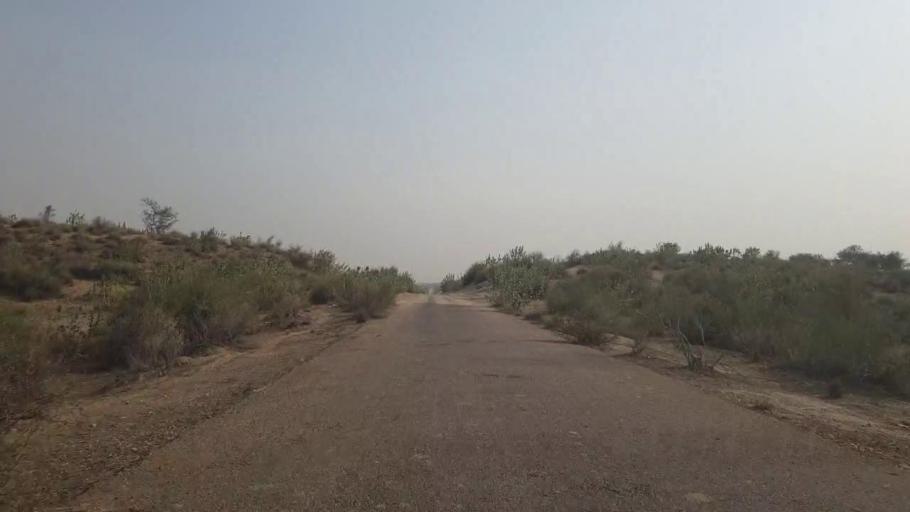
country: PK
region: Sindh
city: Chor
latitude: 25.4436
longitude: 69.9649
